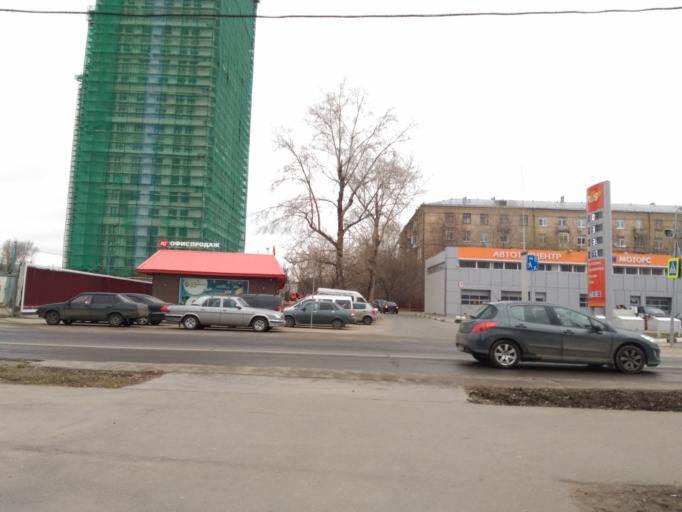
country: RU
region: Moskovskaya
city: Khoroshevo-Mnevniki
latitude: 55.7885
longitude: 37.4760
